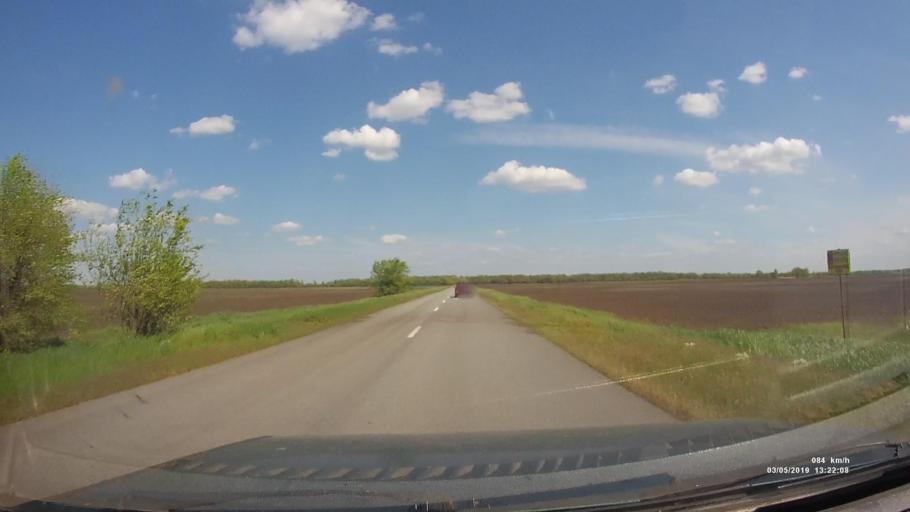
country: RU
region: Rostov
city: Semikarakorsk
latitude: 47.5603
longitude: 40.7606
